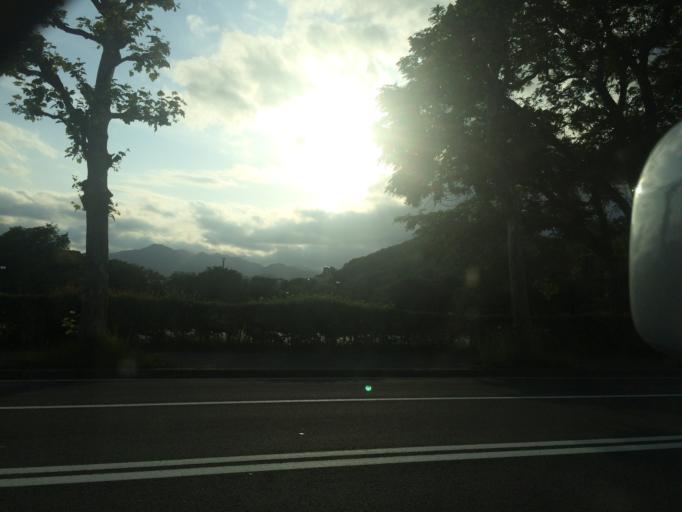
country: JP
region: Hokkaido
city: Sapporo
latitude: 43.0005
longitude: 141.3486
